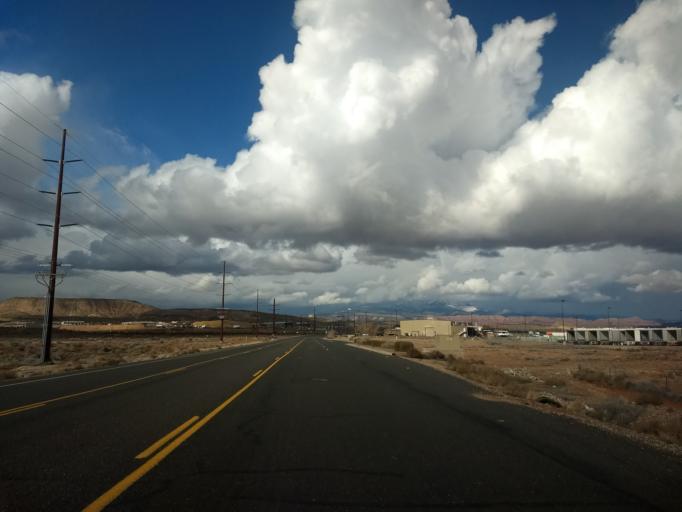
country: US
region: Utah
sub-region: Washington County
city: Saint George
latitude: 37.0245
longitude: -113.5631
